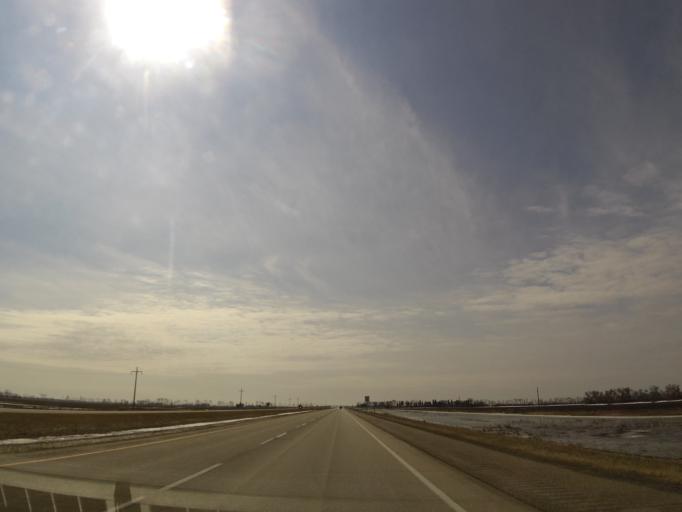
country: US
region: North Dakota
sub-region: Walsh County
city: Grafton
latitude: 48.4035
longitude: -97.1907
